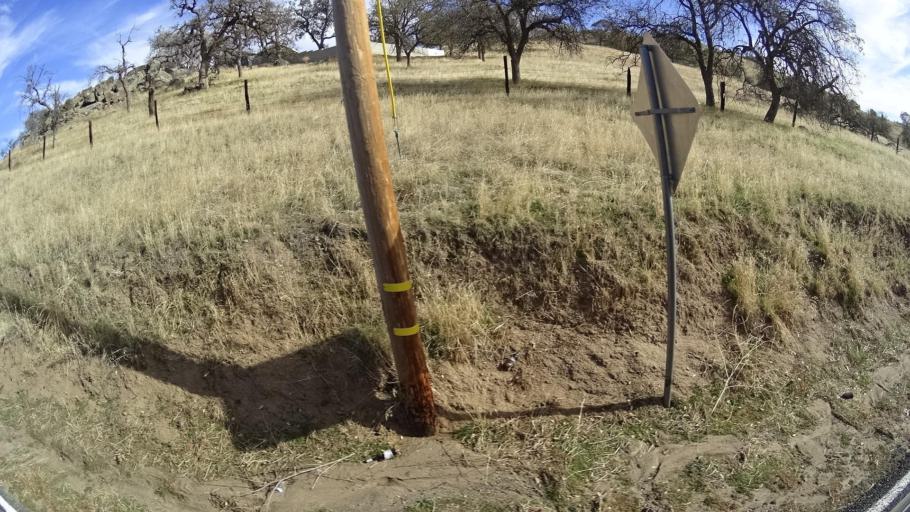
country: US
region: California
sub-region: Kern County
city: Alta Sierra
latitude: 35.6346
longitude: -118.8012
